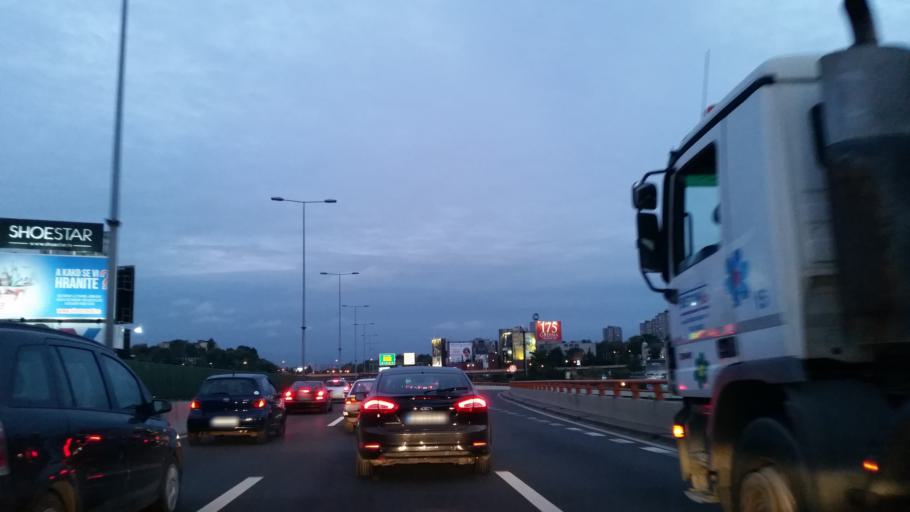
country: RS
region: Central Serbia
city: Belgrade
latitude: 44.8002
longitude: 20.4456
